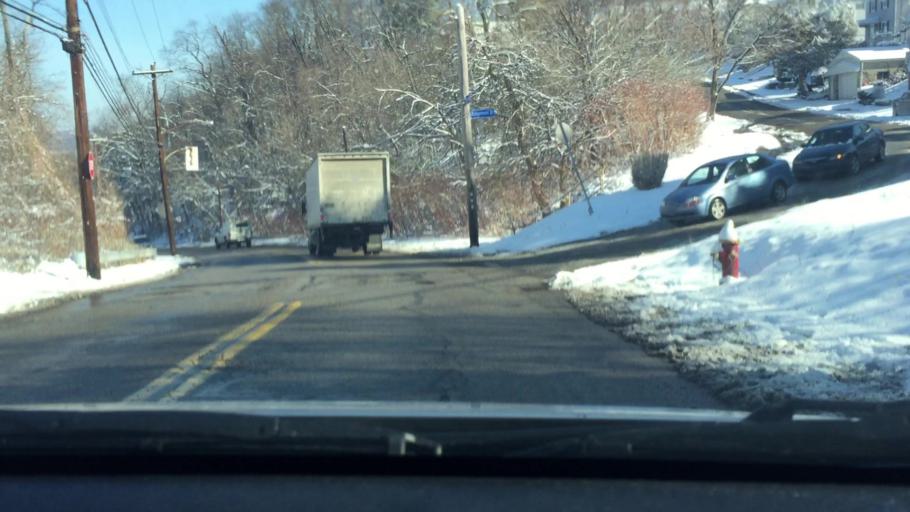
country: US
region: Pennsylvania
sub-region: Allegheny County
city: Green Tree
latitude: 40.4290
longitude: -80.0402
